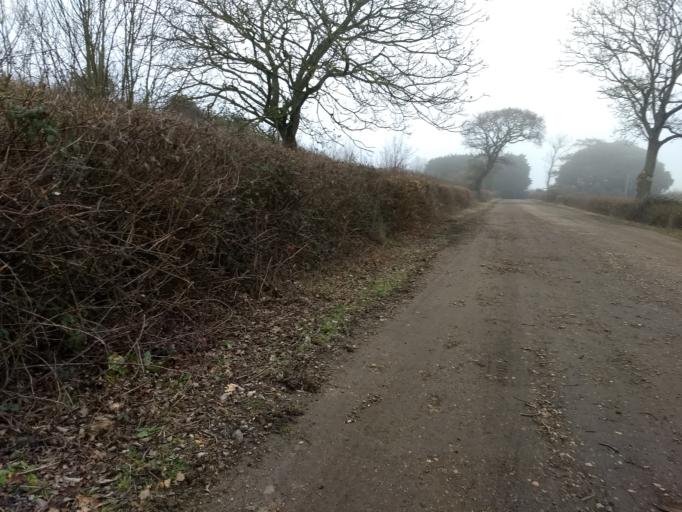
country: GB
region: England
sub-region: Isle of Wight
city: Newport
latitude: 50.7034
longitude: -1.2630
